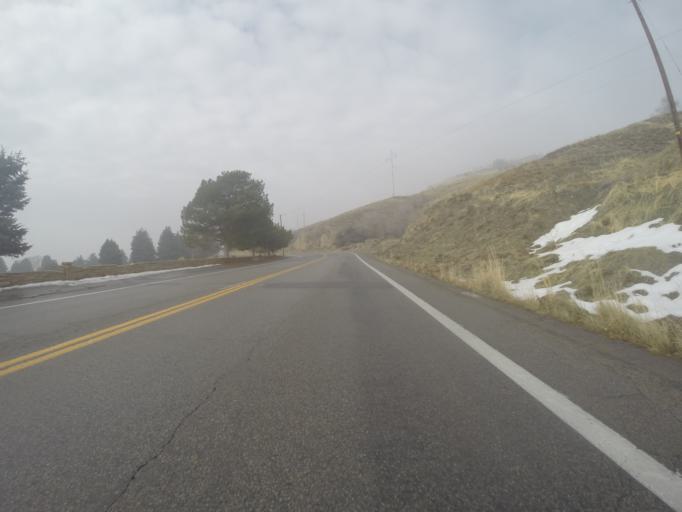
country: US
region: Utah
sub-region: Salt Lake County
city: Salt Lake City
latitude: 40.7792
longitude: -111.8552
